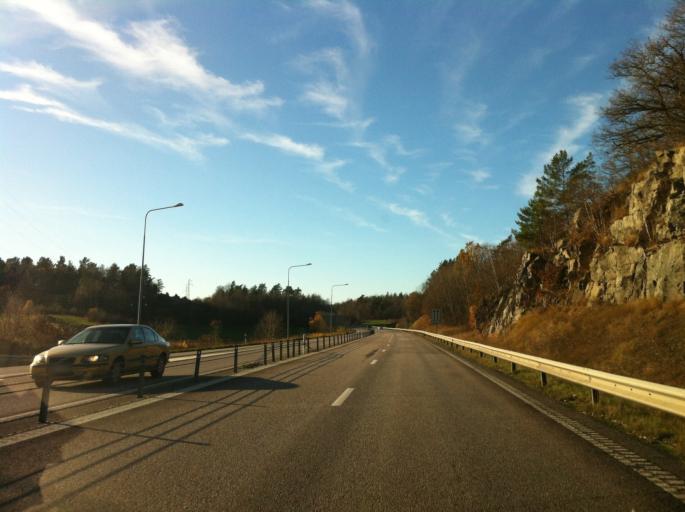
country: SE
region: Blekinge
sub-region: Karlshamns Kommun
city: Karlshamn
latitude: 56.1887
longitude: 14.9265
